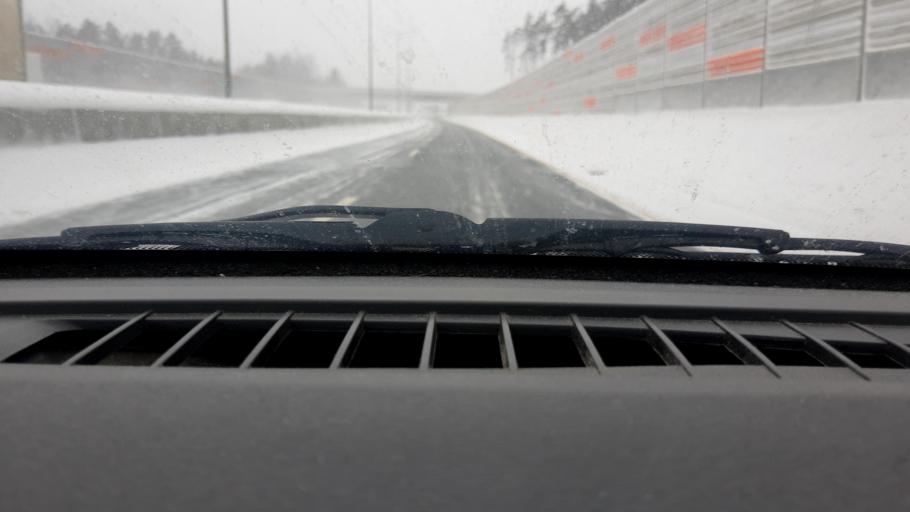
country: RU
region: Moskovskaya
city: Krasnoarmeysk
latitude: 56.0418
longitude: 38.1839
